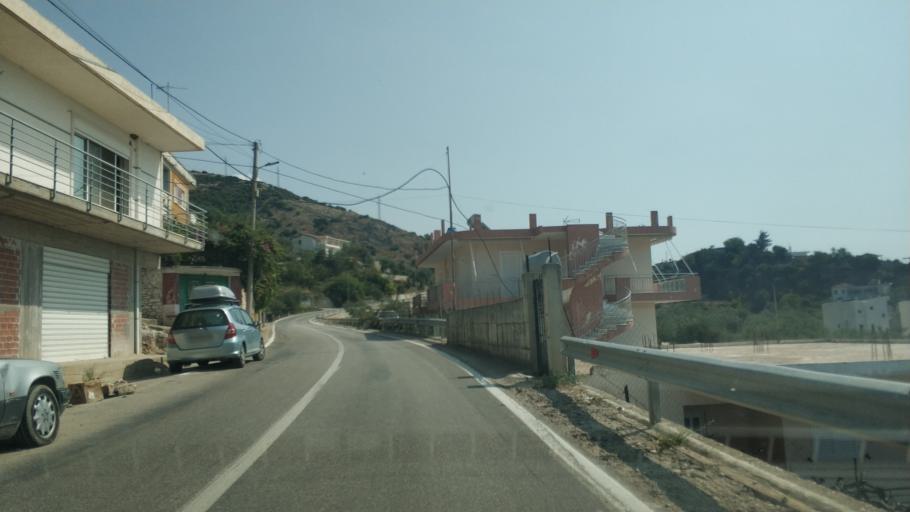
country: AL
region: Vlore
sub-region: Rrethi i Vlores
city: Himare
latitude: 40.0560
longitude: 19.8256
